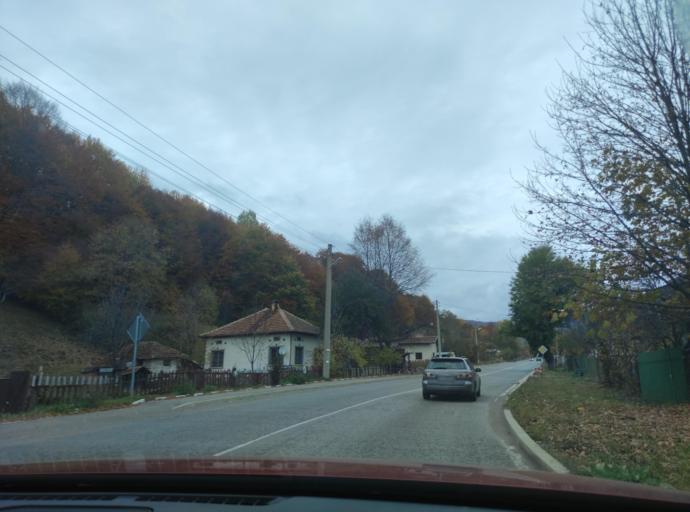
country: BG
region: Sofiya
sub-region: Obshtina Godech
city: Godech
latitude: 43.0820
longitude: 23.1043
